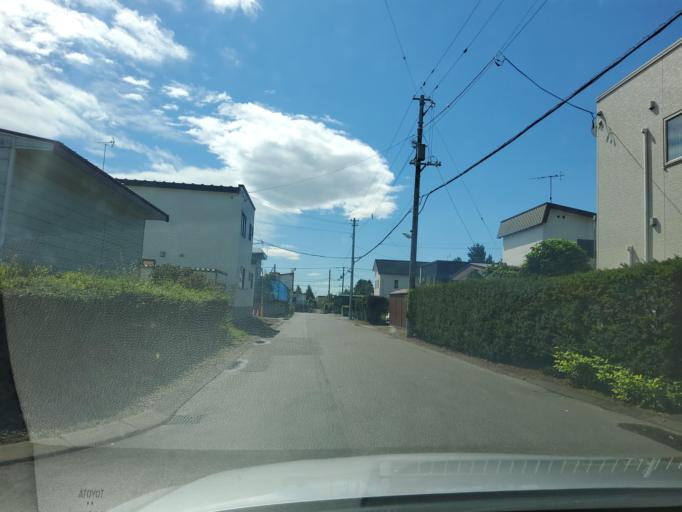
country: JP
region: Hokkaido
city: Otofuke
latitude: 42.9725
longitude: 143.1922
